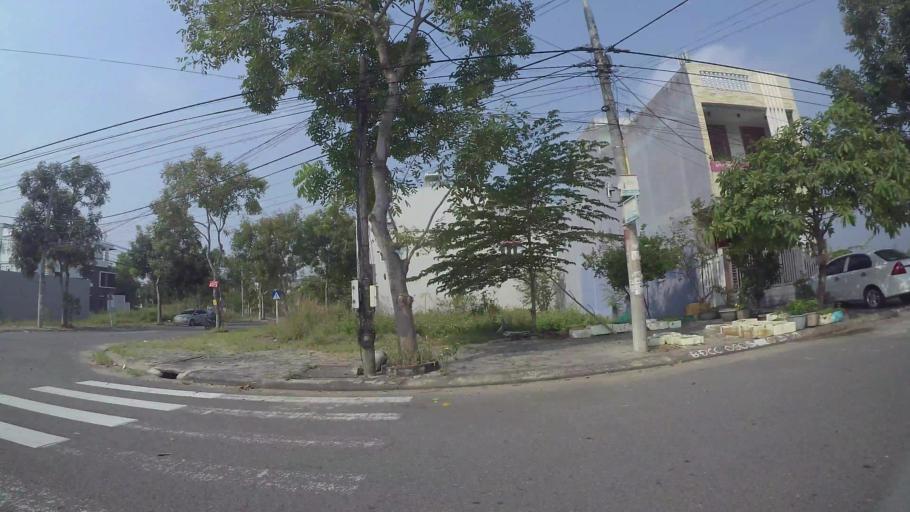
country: VN
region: Da Nang
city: Ngu Hanh Son
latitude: 16.0319
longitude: 108.2408
